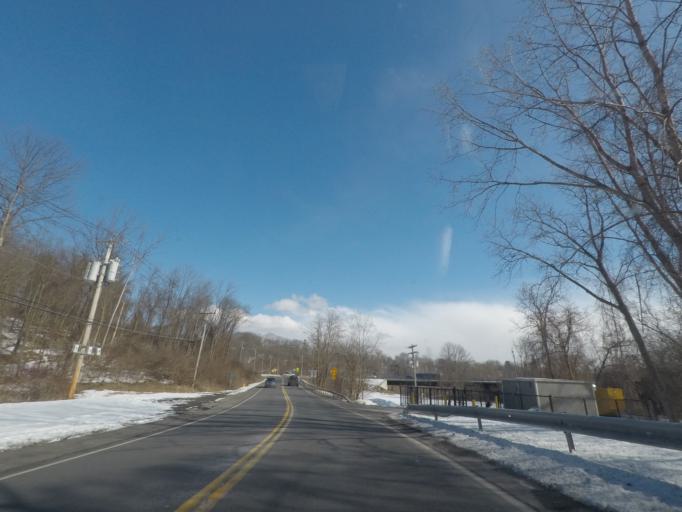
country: US
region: New York
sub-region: Albany County
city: Delmar
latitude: 42.6491
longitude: -73.8504
